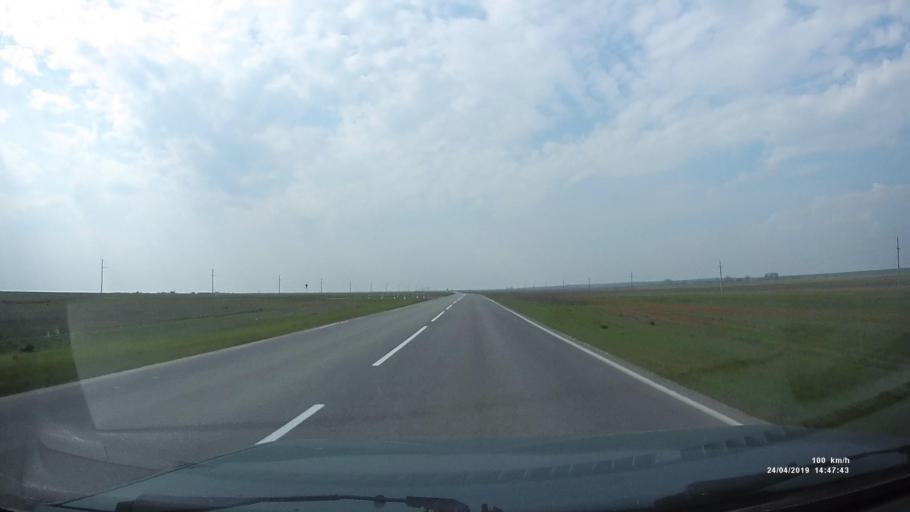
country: RU
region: Rostov
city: Remontnoye
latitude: 46.4941
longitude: 43.7683
